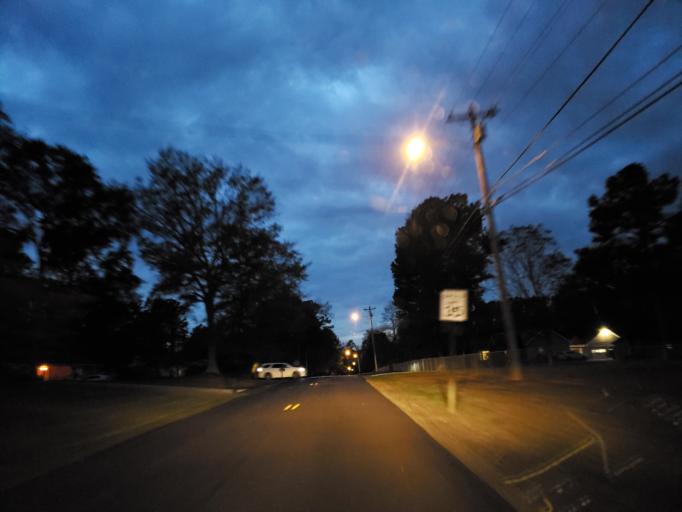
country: US
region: Georgia
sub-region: Cobb County
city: Powder Springs
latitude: 33.8850
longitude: -84.7046
